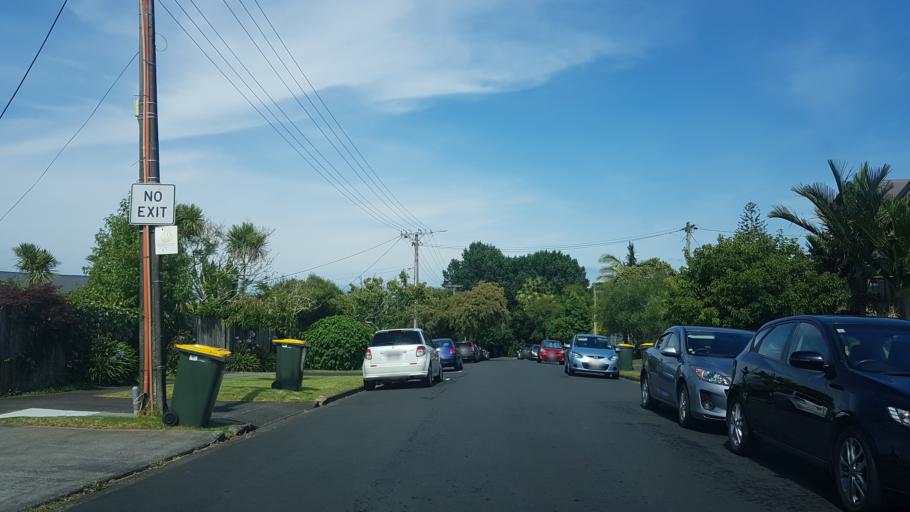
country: NZ
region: Auckland
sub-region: Auckland
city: North Shore
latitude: -36.7957
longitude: 174.7733
